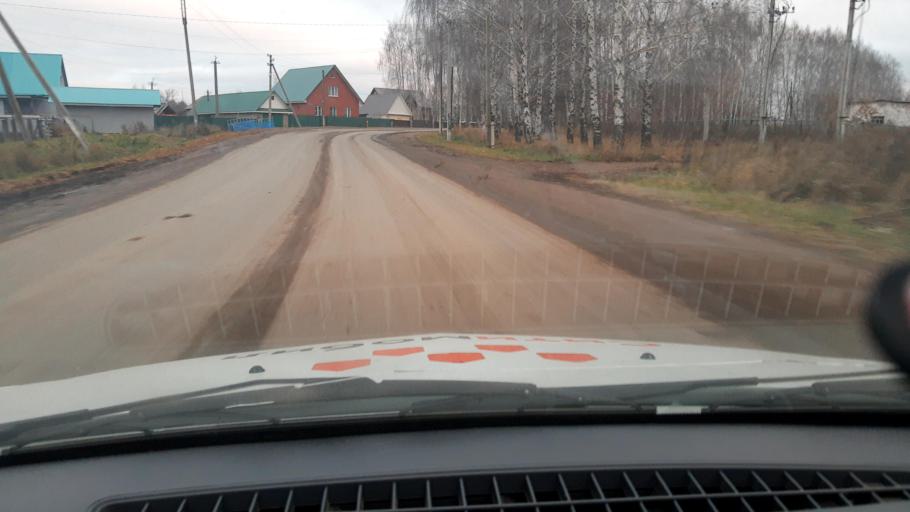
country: RU
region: Bashkortostan
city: Iglino
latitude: 54.8195
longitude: 56.3995
